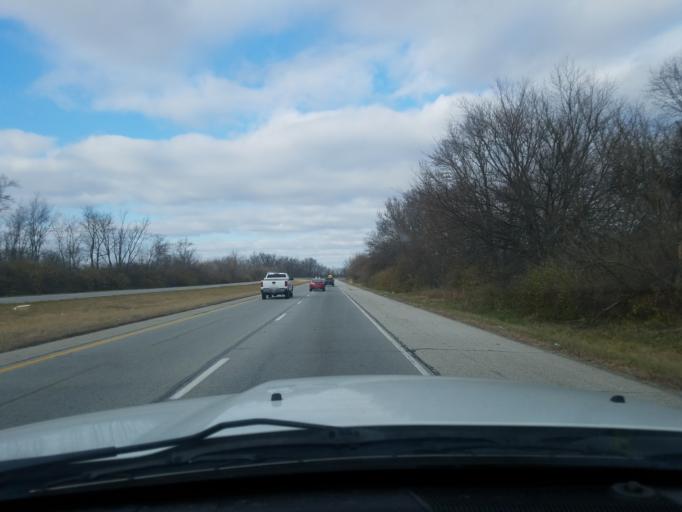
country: US
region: Indiana
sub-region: Marion County
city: Southport
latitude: 39.6455
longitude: -86.2023
